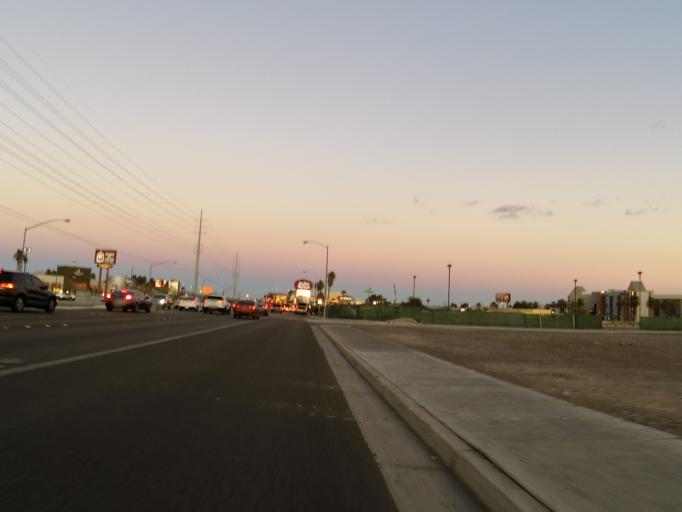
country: US
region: Nevada
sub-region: Clark County
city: Paradise
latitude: 36.1141
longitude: -115.1572
